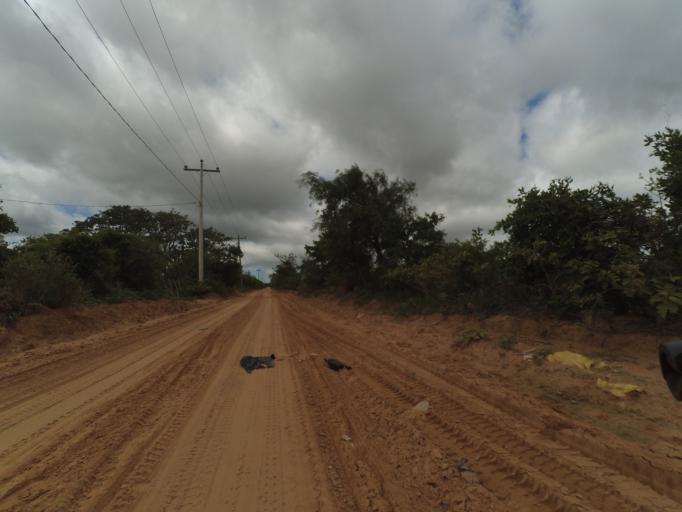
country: BO
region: Santa Cruz
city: Santa Rita
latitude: -17.9082
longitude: -63.2466
